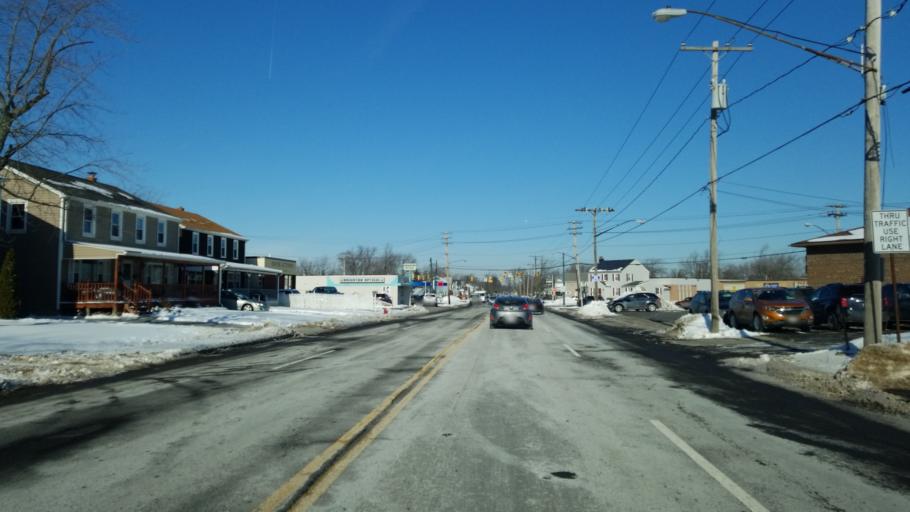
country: US
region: New York
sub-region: Erie County
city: Tonawanda
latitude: 42.9904
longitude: -78.8392
